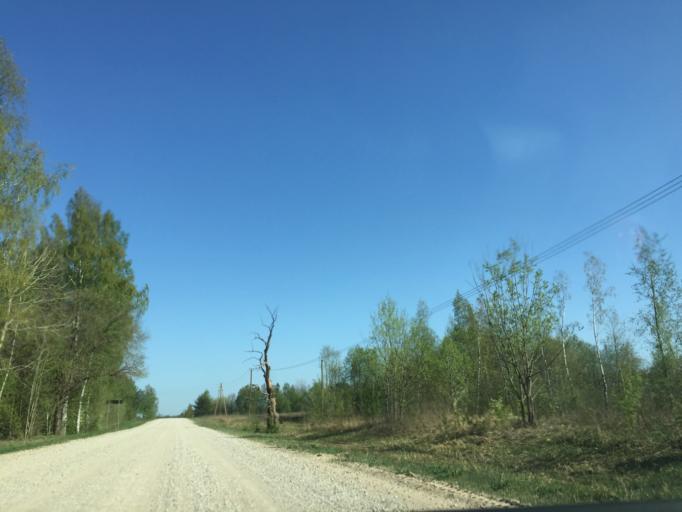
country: LV
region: Skriveri
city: Skriveri
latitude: 56.8374
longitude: 25.1122
